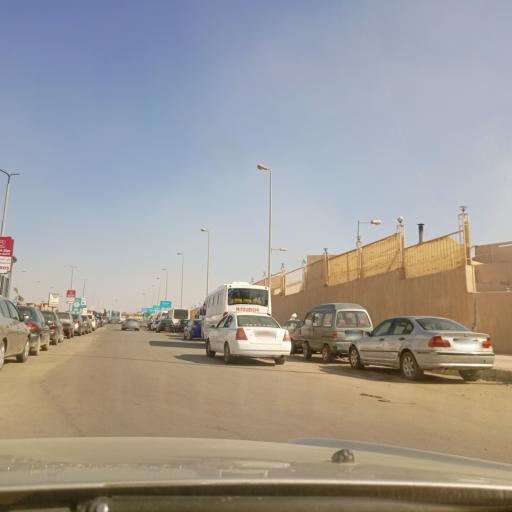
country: EG
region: Muhafazat al Qahirah
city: Cairo
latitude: 30.0187
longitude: 31.4337
